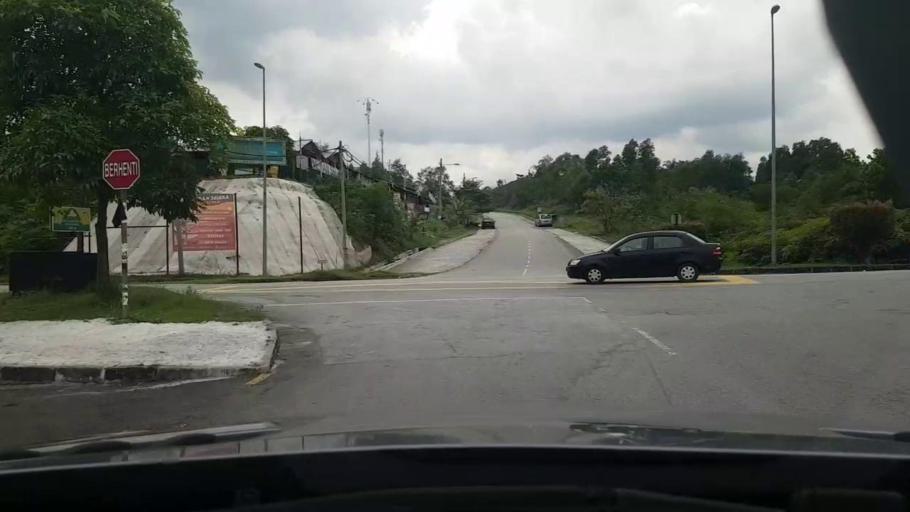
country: MY
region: Selangor
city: Subang Jaya
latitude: 2.9808
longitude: 101.6194
